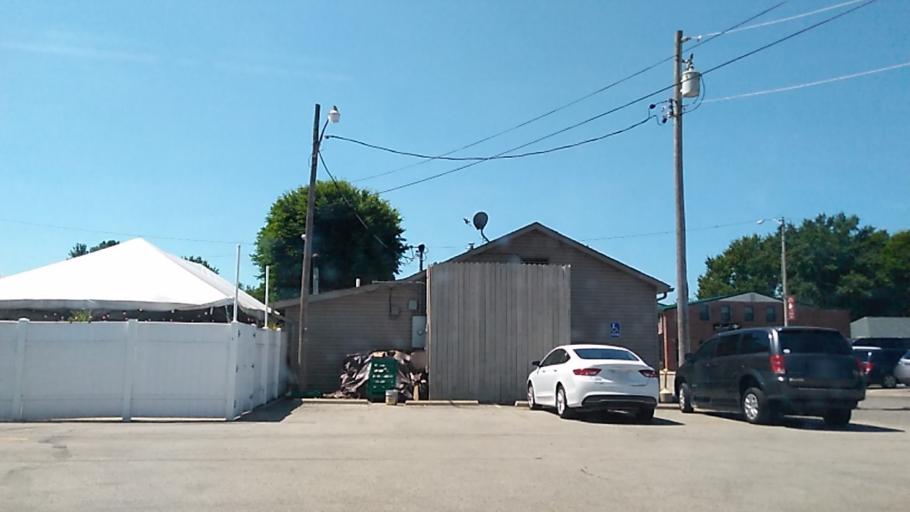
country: US
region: Illinois
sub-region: Monroe County
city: Columbia
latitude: 38.4478
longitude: -90.2037
